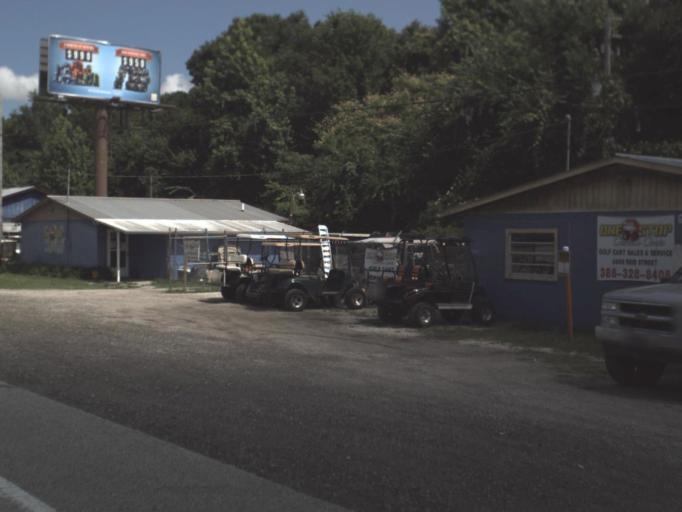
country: US
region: Florida
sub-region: Putnam County
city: Palatka
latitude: 29.6611
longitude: -81.6769
